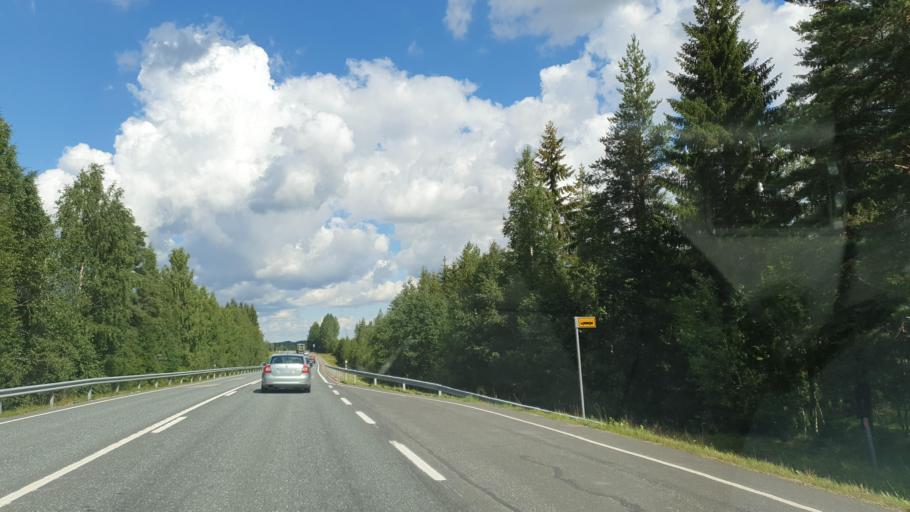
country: FI
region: Kainuu
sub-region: Kajaani
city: Kajaani
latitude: 64.0532
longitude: 27.4533
